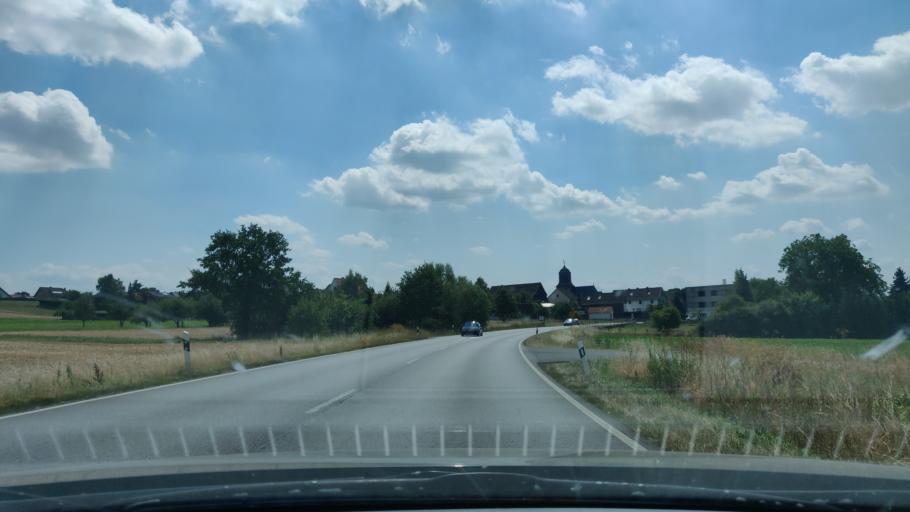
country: DE
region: Hesse
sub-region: Regierungsbezirk Kassel
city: Wabern
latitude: 51.0713
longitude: 9.3792
